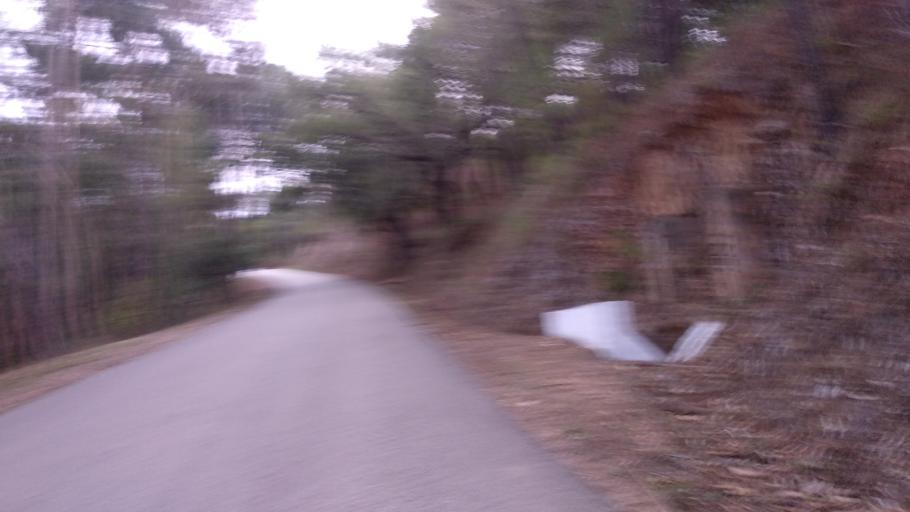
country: PT
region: Faro
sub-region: Sao Bras de Alportel
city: Sao Bras de Alportel
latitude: 37.1819
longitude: -7.9133
